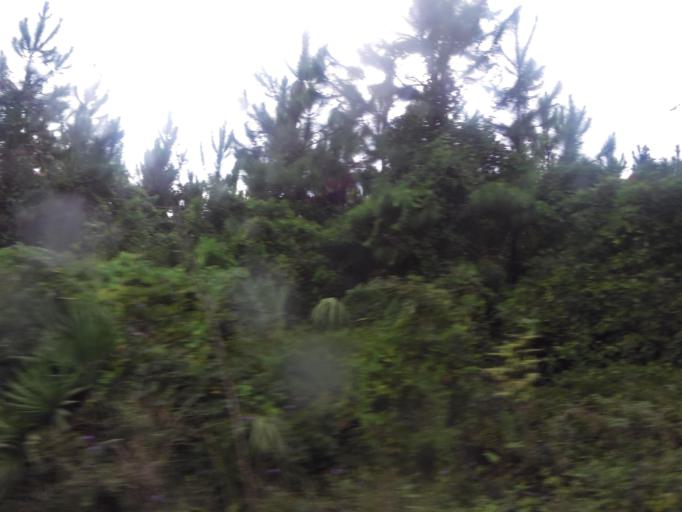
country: US
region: Florida
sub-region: Flagler County
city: Palm Coast
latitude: 29.5847
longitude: -81.3455
